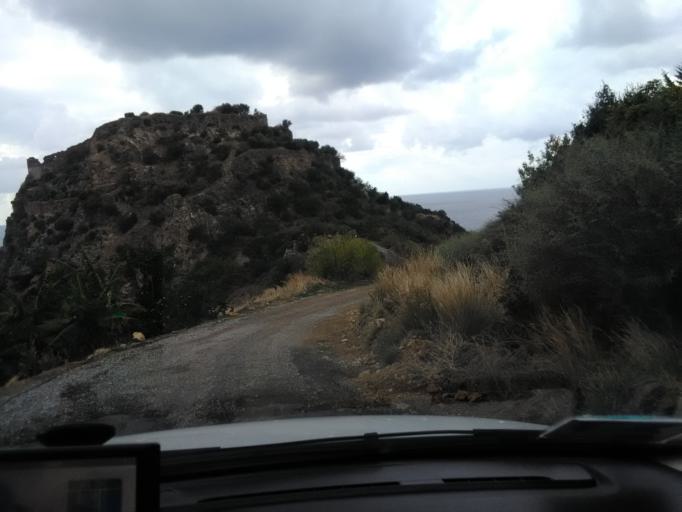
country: TR
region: Antalya
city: Gazipasa
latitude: 36.1572
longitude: 32.4179
